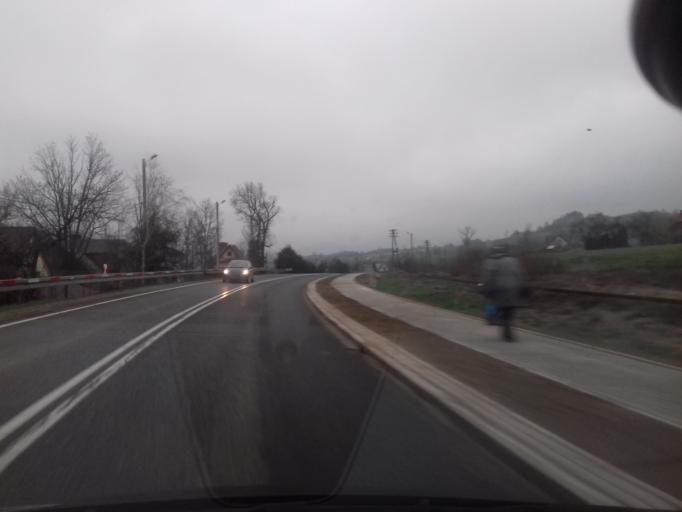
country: PL
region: Lesser Poland Voivodeship
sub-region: Powiat limanowski
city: Kasina Wielka
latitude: 49.6979
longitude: 20.1264
